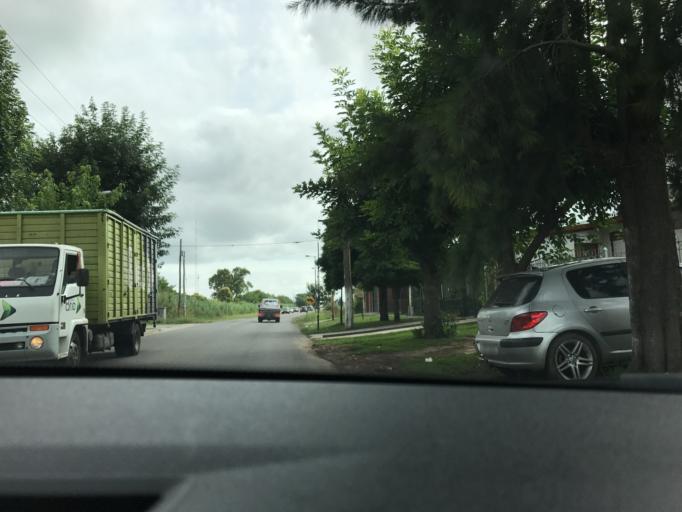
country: AR
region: Buenos Aires
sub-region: Partido de La Plata
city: La Plata
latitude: -34.8468
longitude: -58.0775
